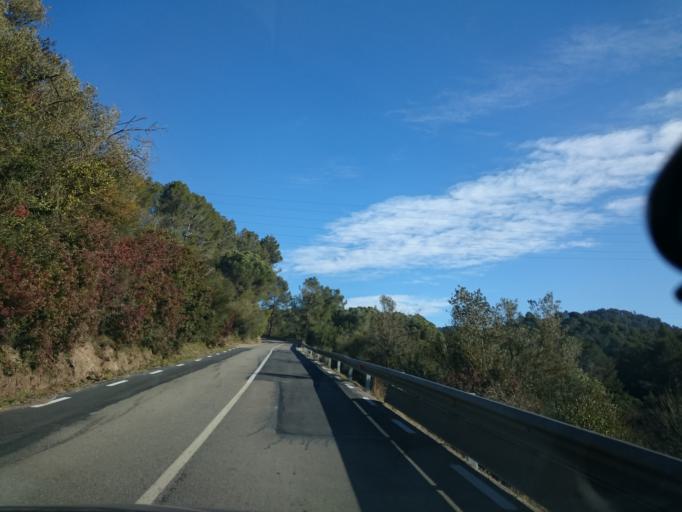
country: ES
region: Catalonia
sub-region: Provincia de Barcelona
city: Molins de Rei
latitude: 41.4221
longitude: 2.0305
